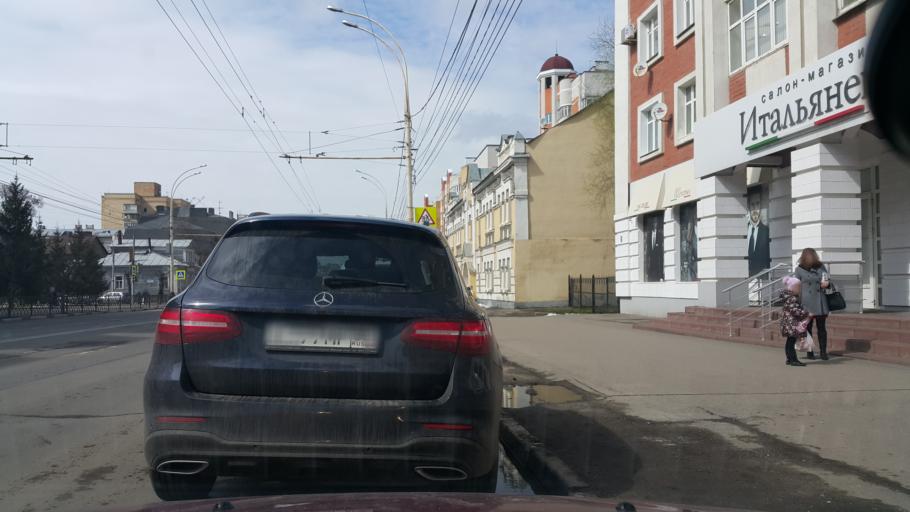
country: RU
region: Tambov
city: Tambov
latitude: 52.7095
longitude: 41.4661
